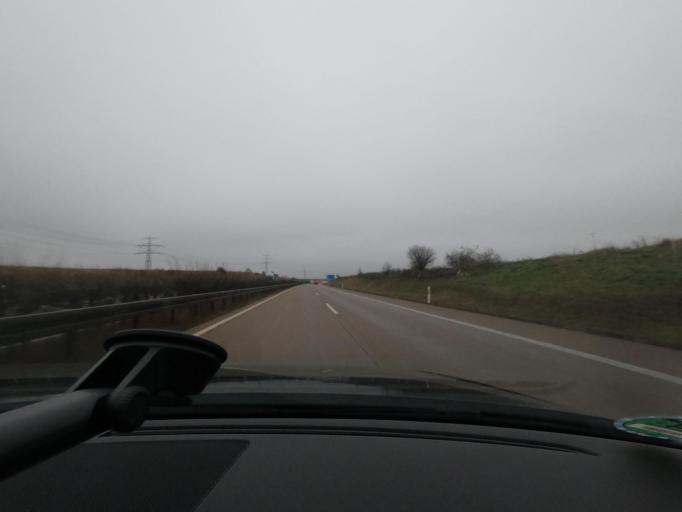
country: DE
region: Thuringia
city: Alkersleben
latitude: 50.8446
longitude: 11.0108
